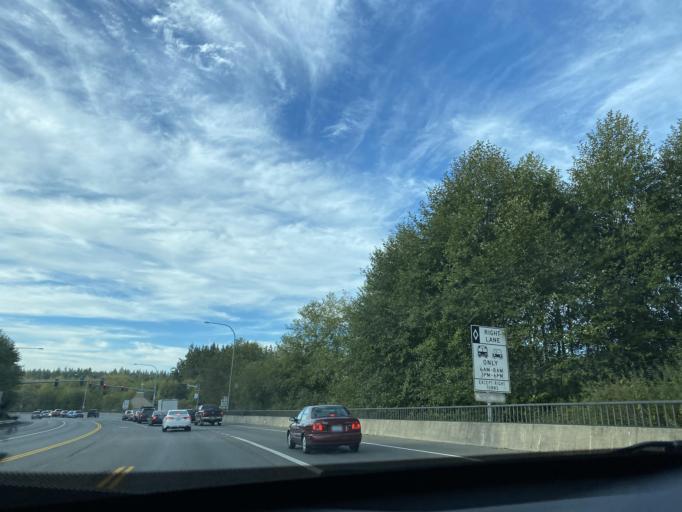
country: US
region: Washington
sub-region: Kitsap County
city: Poulsbo
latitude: 47.7457
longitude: -122.6388
